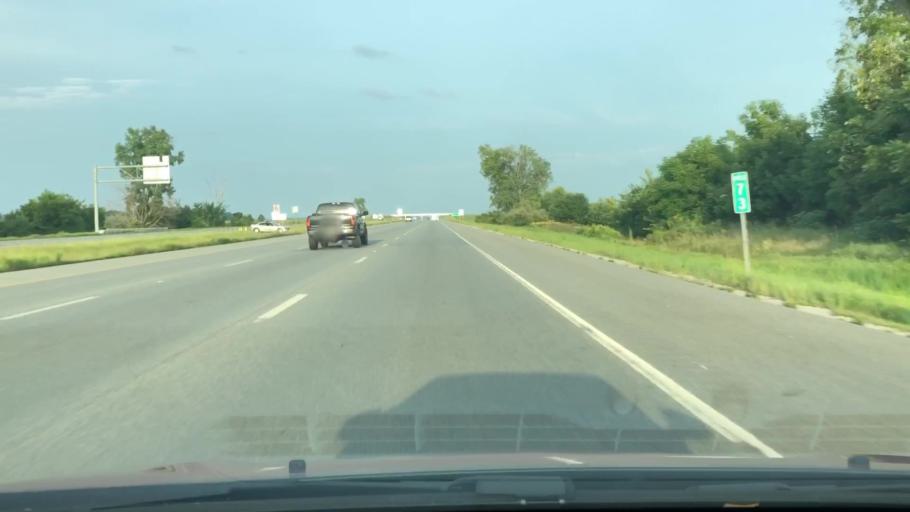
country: US
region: Ohio
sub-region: Madison County
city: Choctaw Lake
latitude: 39.9419
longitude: -83.4882
